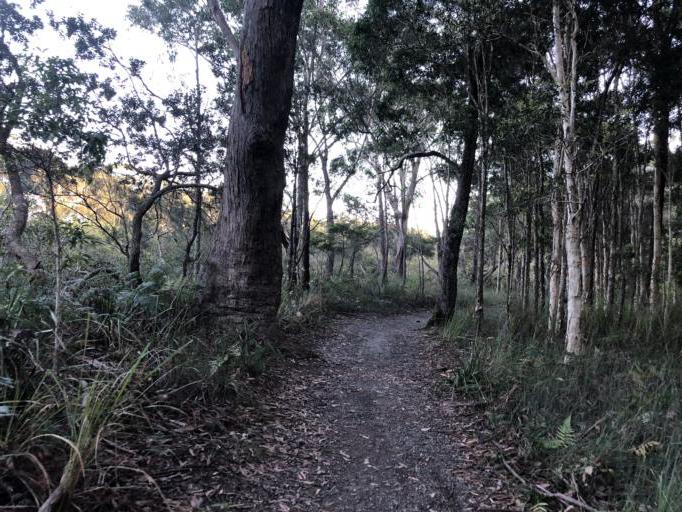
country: AU
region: New South Wales
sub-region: Coffs Harbour
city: Coffs Harbour
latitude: -30.3029
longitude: 153.1288
